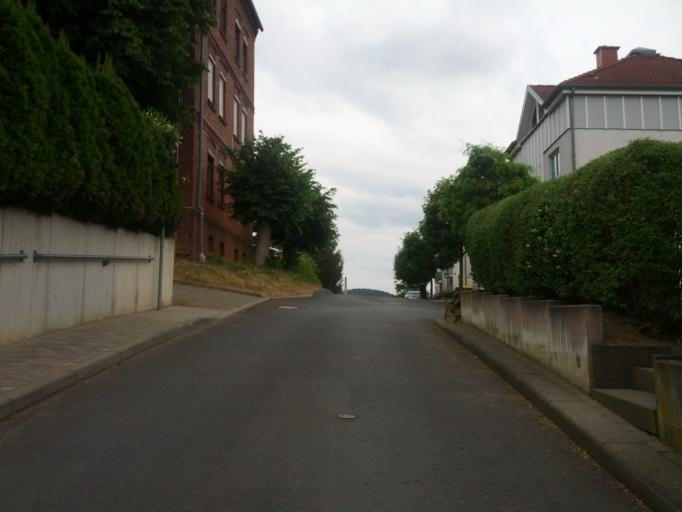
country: DE
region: Thuringia
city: Eisenach
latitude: 50.9856
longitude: 10.3305
